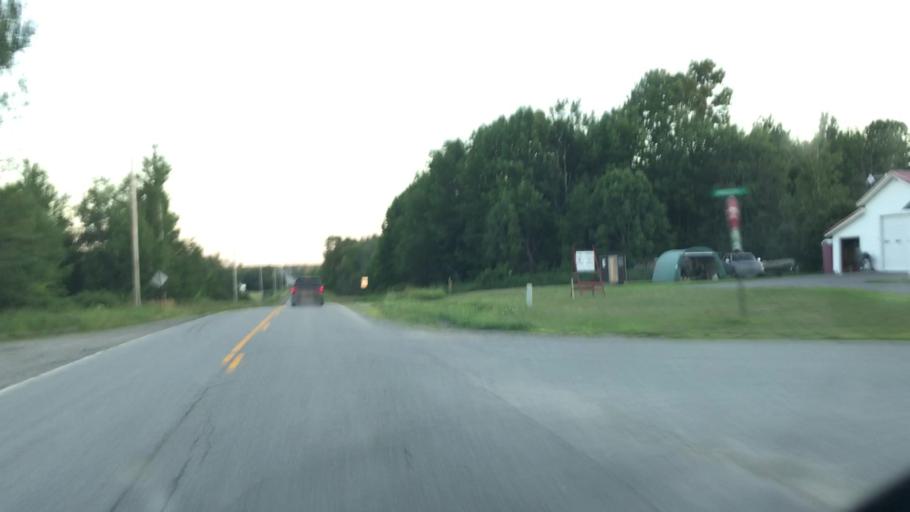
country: US
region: Maine
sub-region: Penobscot County
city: Medway
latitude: 45.6154
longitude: -68.3035
